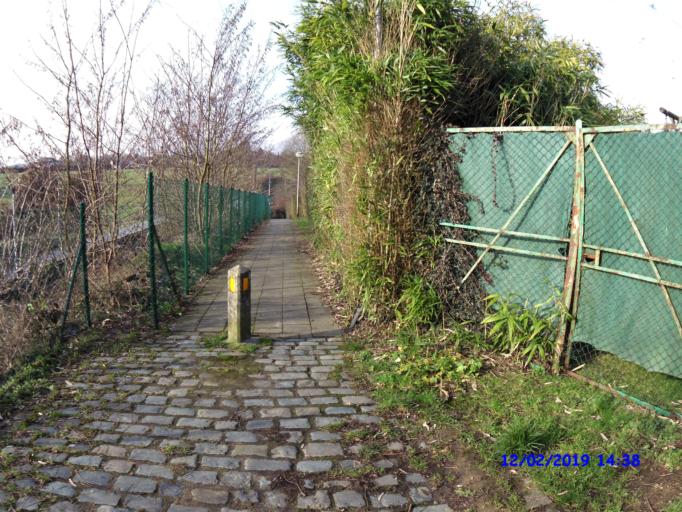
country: BE
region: Flanders
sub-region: Provincie Vlaams-Brabant
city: Sint-Genesius-Rode
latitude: 50.7391
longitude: 4.3708
